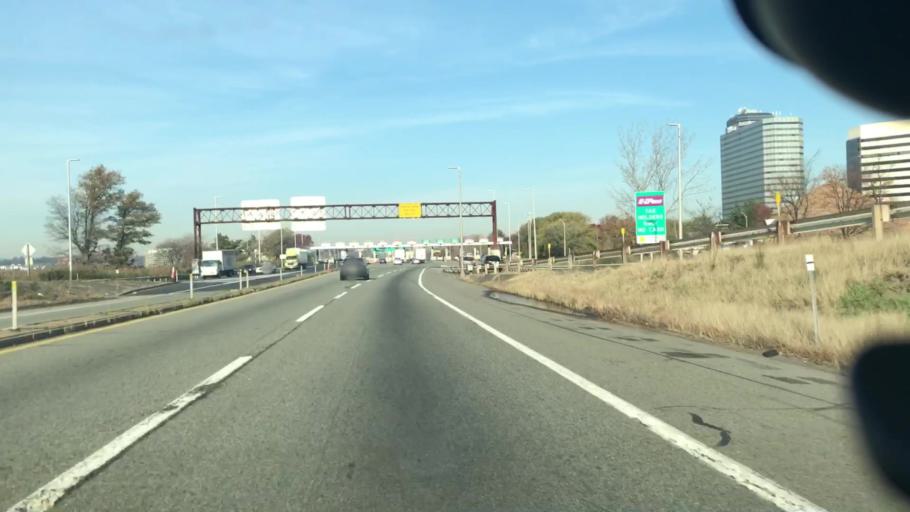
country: US
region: New Jersey
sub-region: Hudson County
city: Secaucus
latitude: 40.8018
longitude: -74.0757
